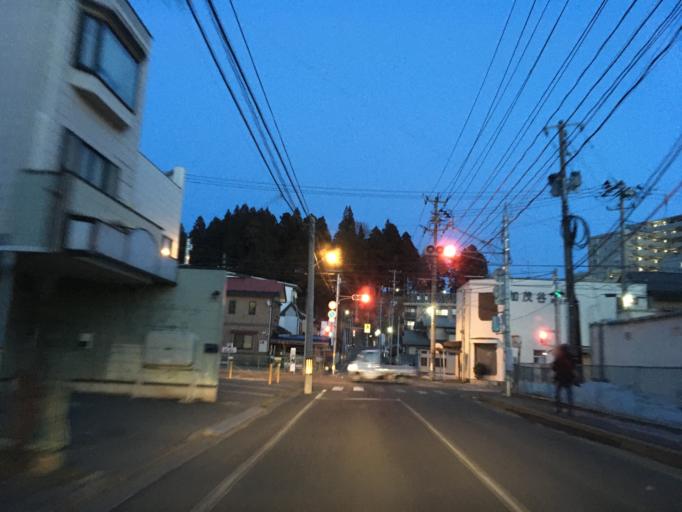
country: JP
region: Iwate
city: Morioka-shi
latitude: 39.7030
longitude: 141.1646
